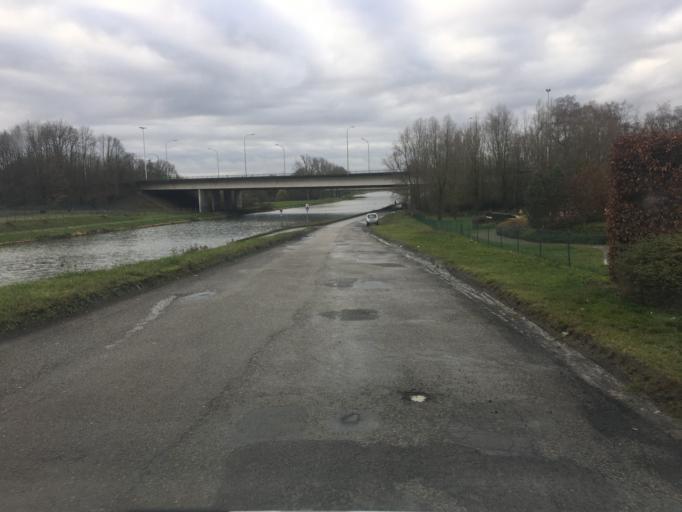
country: BE
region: Wallonia
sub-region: Province du Hainaut
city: Manage
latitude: 50.5124
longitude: 4.2129
